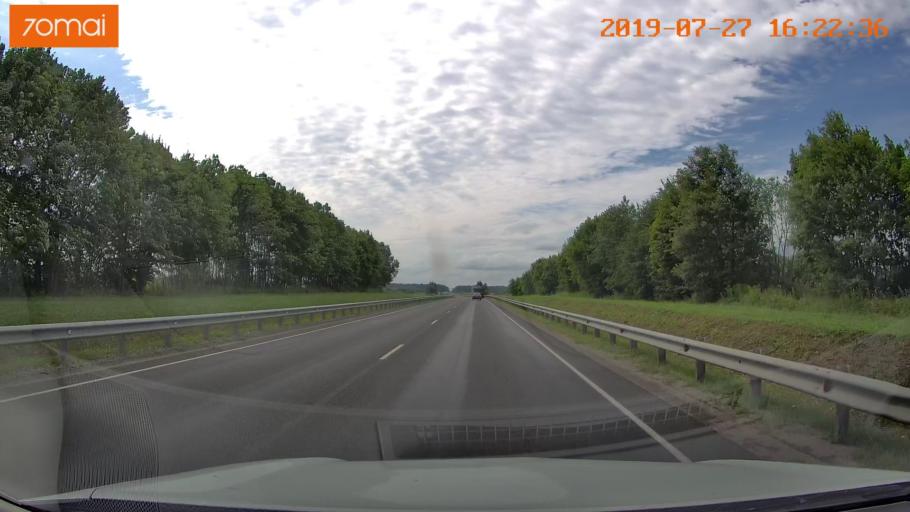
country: RU
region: Kaliningrad
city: Chernyakhovsk
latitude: 54.6285
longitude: 21.4917
